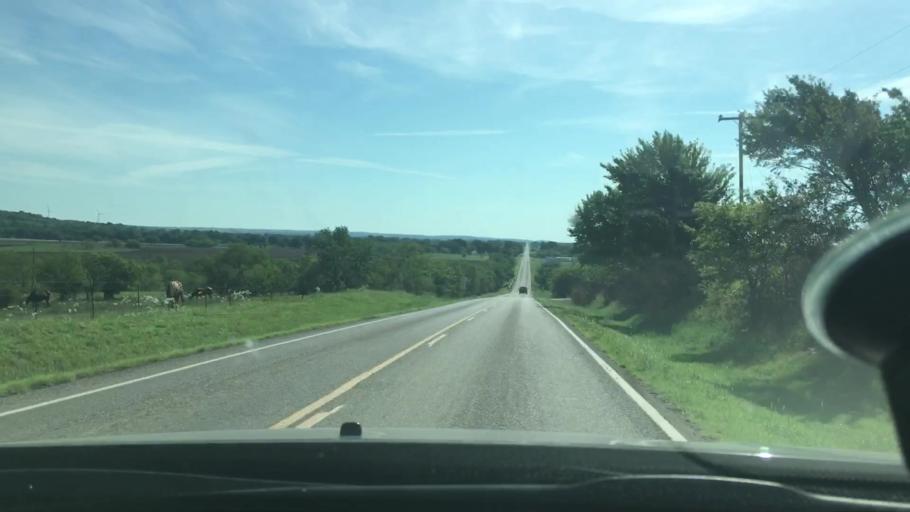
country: US
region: Oklahoma
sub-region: Carter County
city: Lone Grove
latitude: 34.3327
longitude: -97.2146
